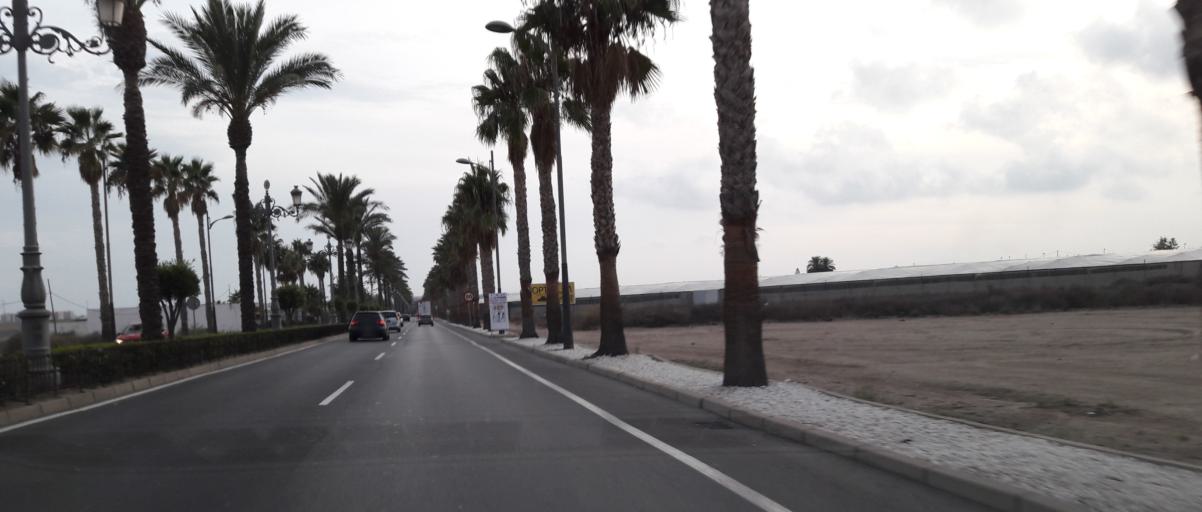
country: ES
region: Andalusia
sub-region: Provincia de Almeria
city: Aguadulce
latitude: 36.7984
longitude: -2.6020
